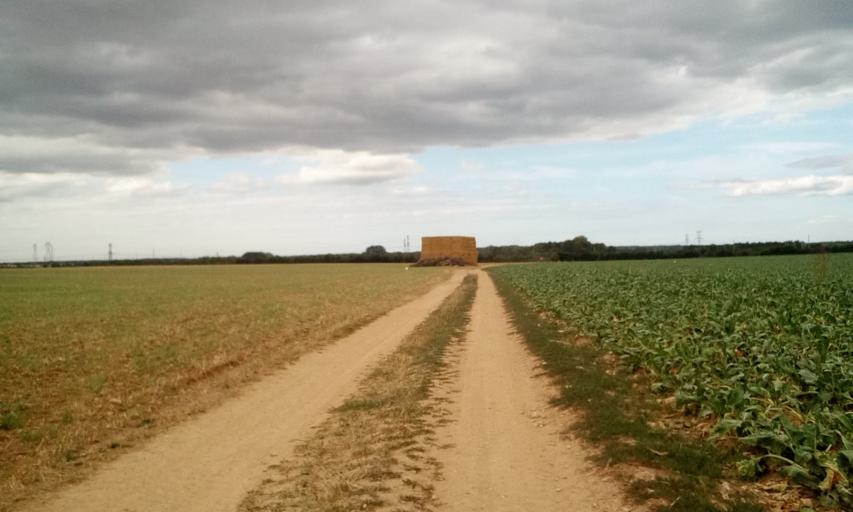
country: FR
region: Lower Normandy
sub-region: Departement du Calvados
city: Bellengreville
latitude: 49.1205
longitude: -0.2243
